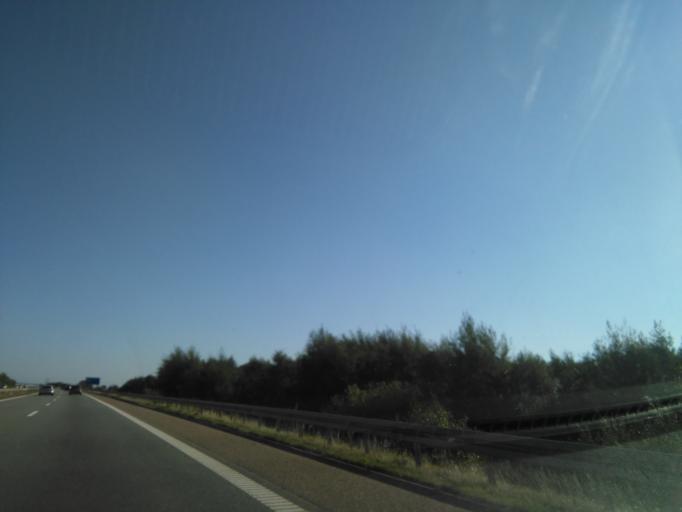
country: DK
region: Central Jutland
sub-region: Arhus Kommune
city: Hjortshoj
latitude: 56.2410
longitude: 10.2861
